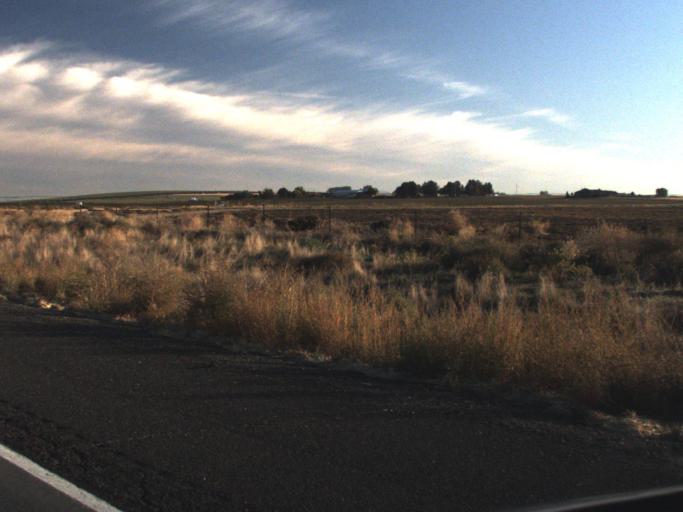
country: US
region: Washington
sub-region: Franklin County
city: Pasco
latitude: 46.3115
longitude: -119.0930
